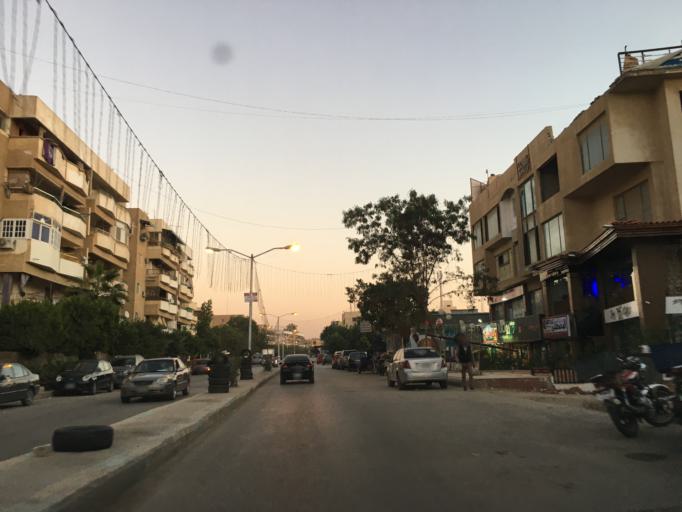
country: EG
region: Al Jizah
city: Madinat Sittah Uktubar
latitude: 29.9842
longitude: 30.9381
